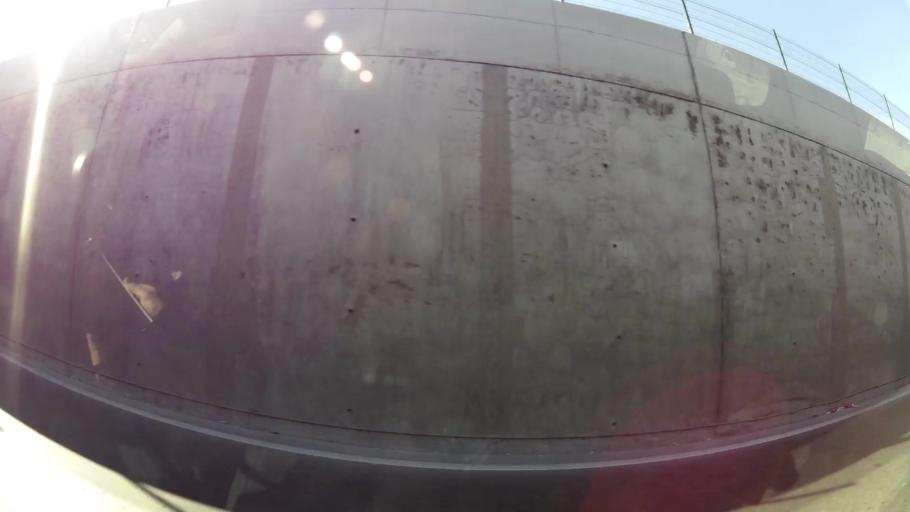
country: CL
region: Santiago Metropolitan
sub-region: Provincia de Santiago
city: La Pintana
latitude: -33.5425
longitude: -70.6329
